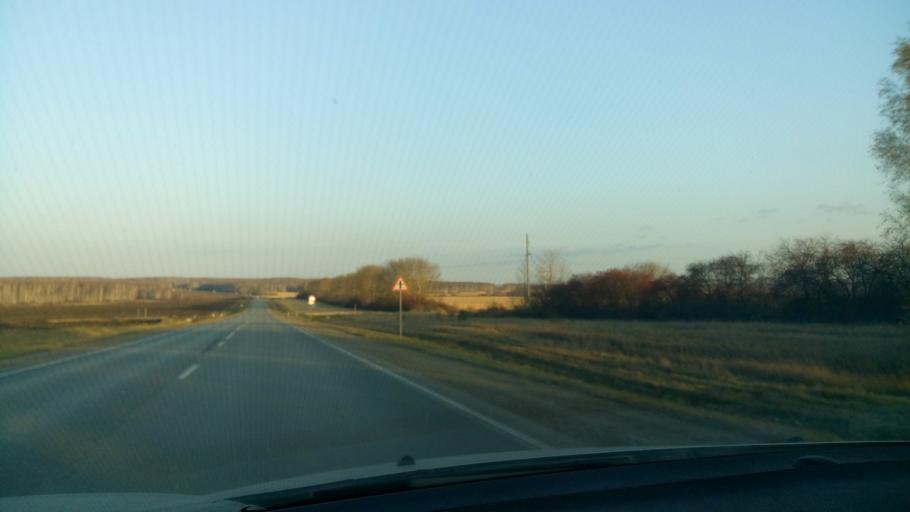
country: RU
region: Sverdlovsk
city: Yelanskiy
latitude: 56.7592
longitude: 62.3721
